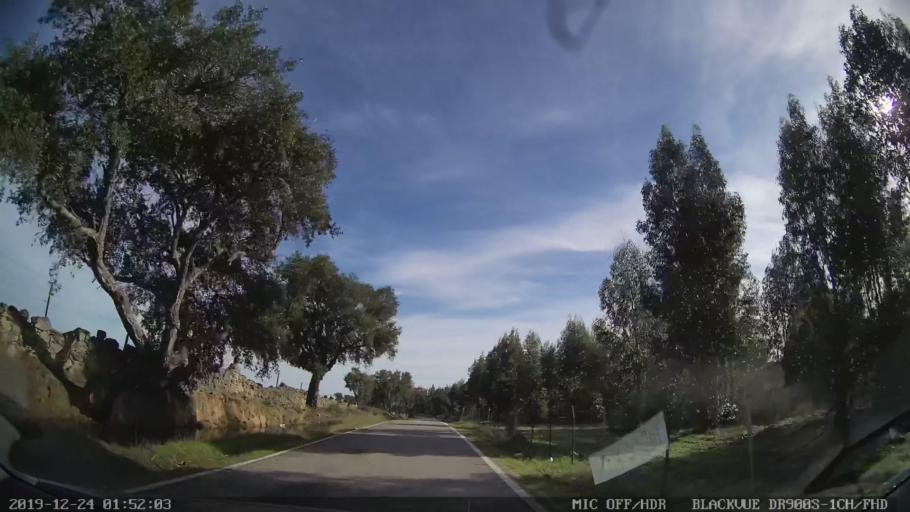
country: PT
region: Portalegre
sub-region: Nisa
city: Nisa
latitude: 39.4935
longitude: -7.7506
